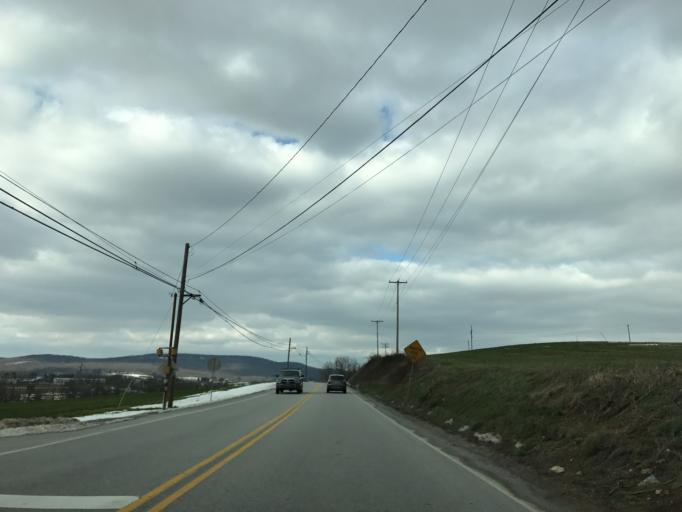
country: US
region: Pennsylvania
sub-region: York County
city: Parkville
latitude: 39.8118
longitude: -76.9448
